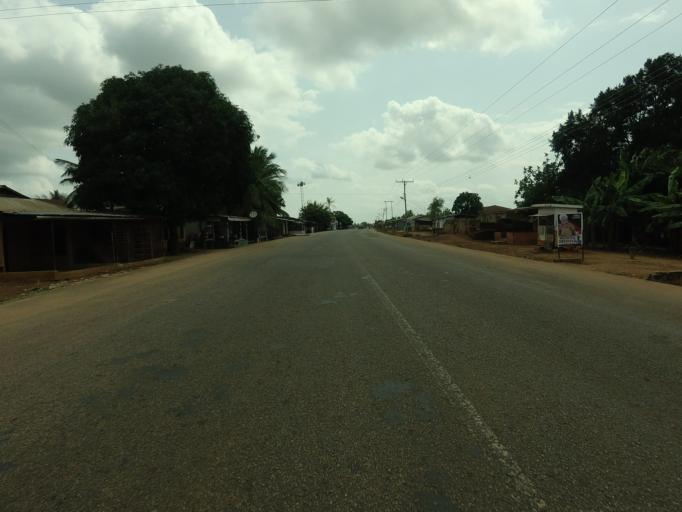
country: TG
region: Maritime
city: Lome
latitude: 6.2220
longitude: 1.0347
